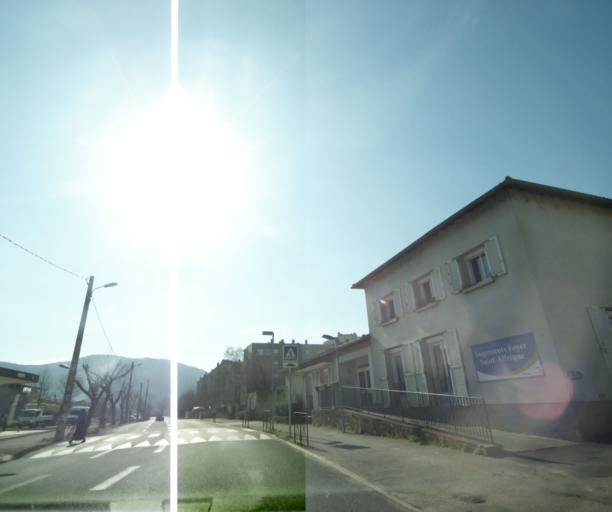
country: FR
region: Midi-Pyrenees
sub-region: Departement de l'Aveyron
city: Saint-Affrique
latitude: 43.9551
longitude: 2.8904
